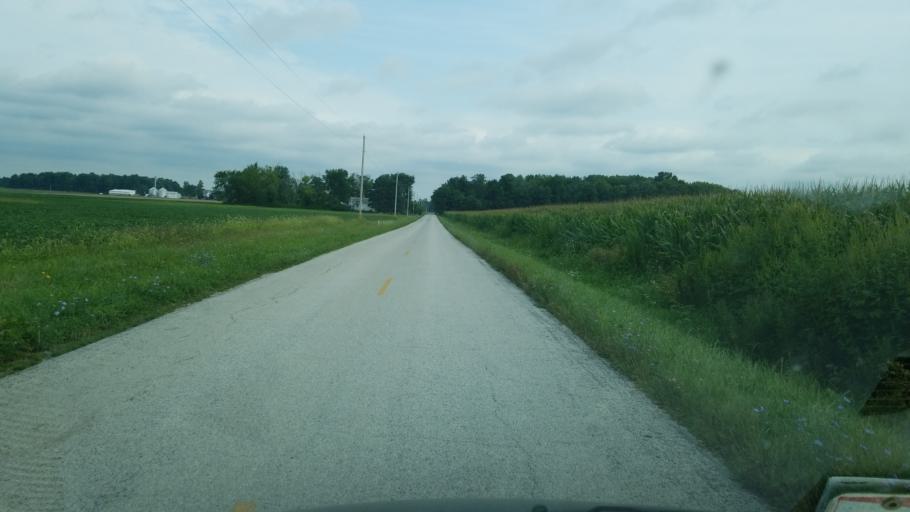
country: US
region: Ohio
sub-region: Seneca County
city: Tiffin
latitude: 41.1734
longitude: -83.1030
